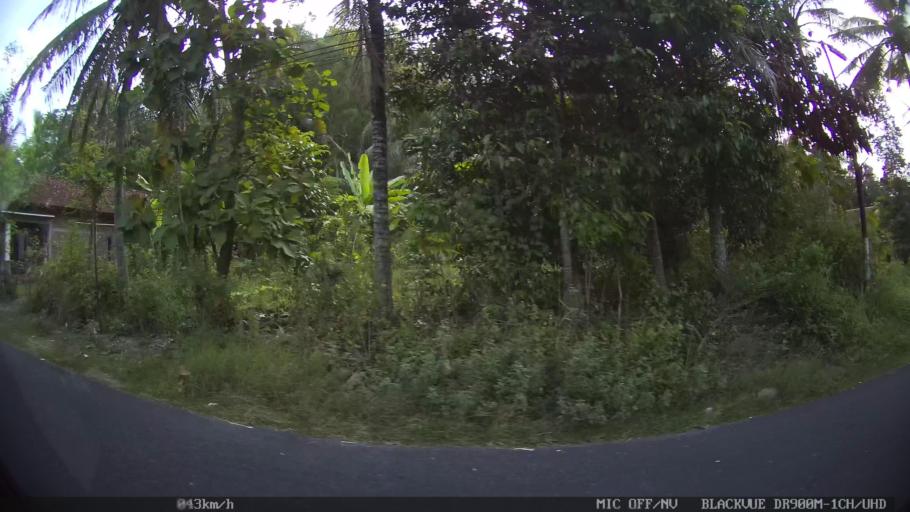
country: ID
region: Daerah Istimewa Yogyakarta
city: Bantul
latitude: -7.8598
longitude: 110.3198
